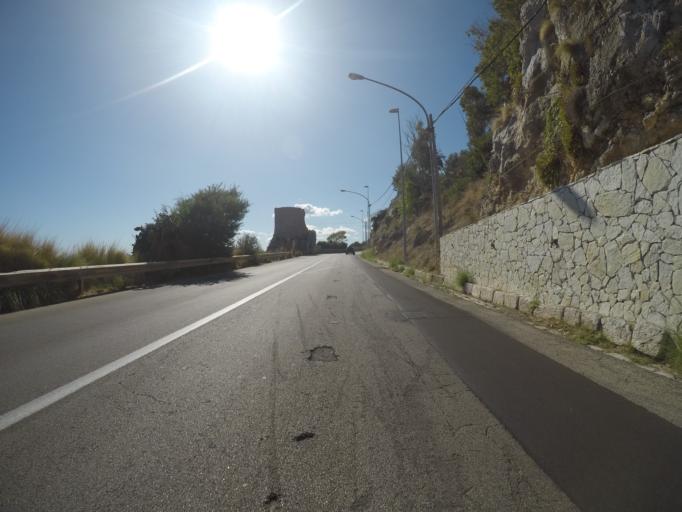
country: IT
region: Sicily
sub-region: Palermo
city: Palermo
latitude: 38.1796
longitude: 13.3659
